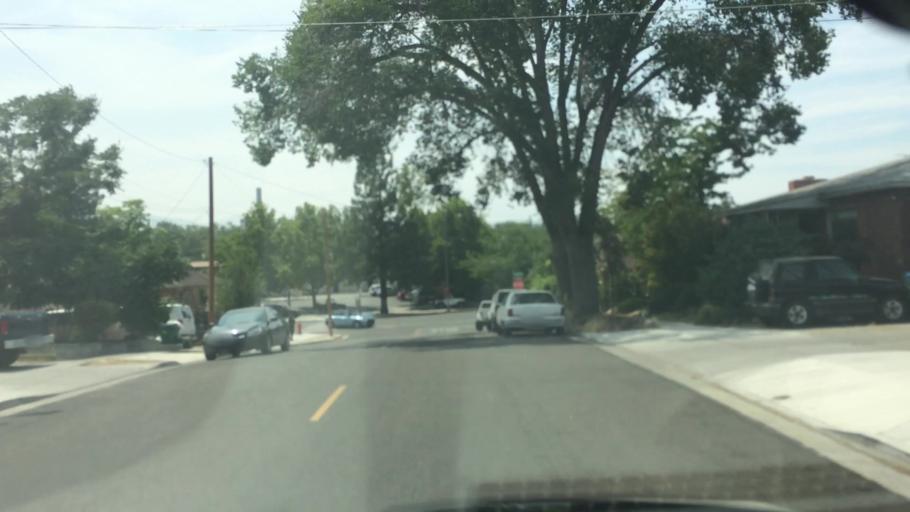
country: US
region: Nevada
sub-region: Washoe County
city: Reno
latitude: 39.5164
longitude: -119.8060
